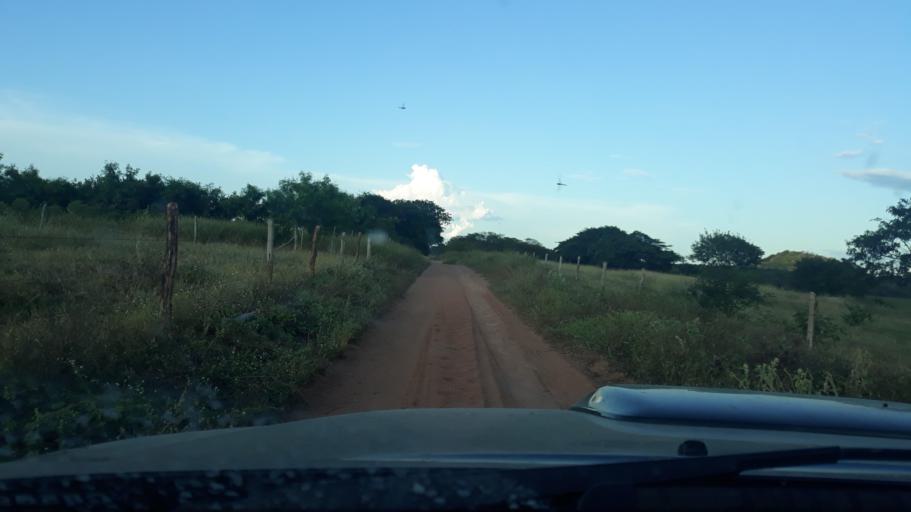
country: BR
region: Bahia
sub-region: Riacho De Santana
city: Riacho de Santana
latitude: -13.8608
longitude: -43.0699
